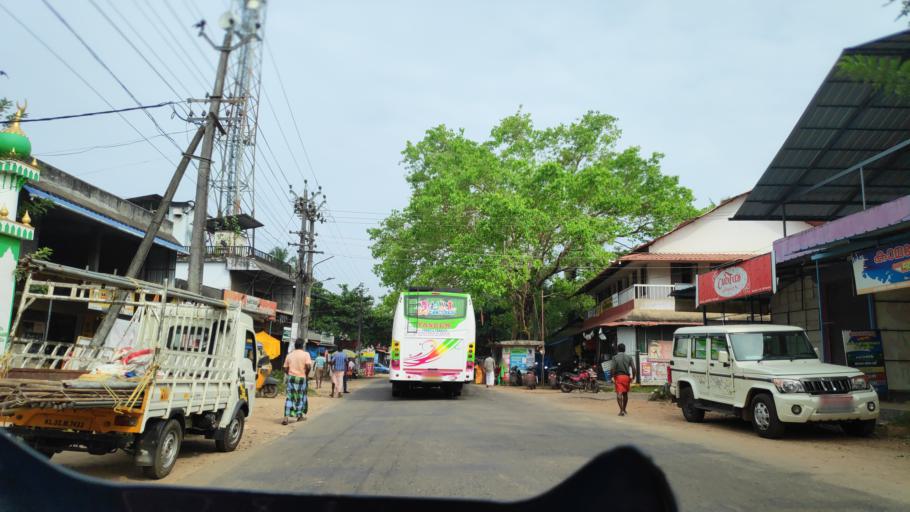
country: IN
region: Kerala
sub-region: Alappuzha
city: Kutiatodu
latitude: 9.8159
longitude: 76.3513
